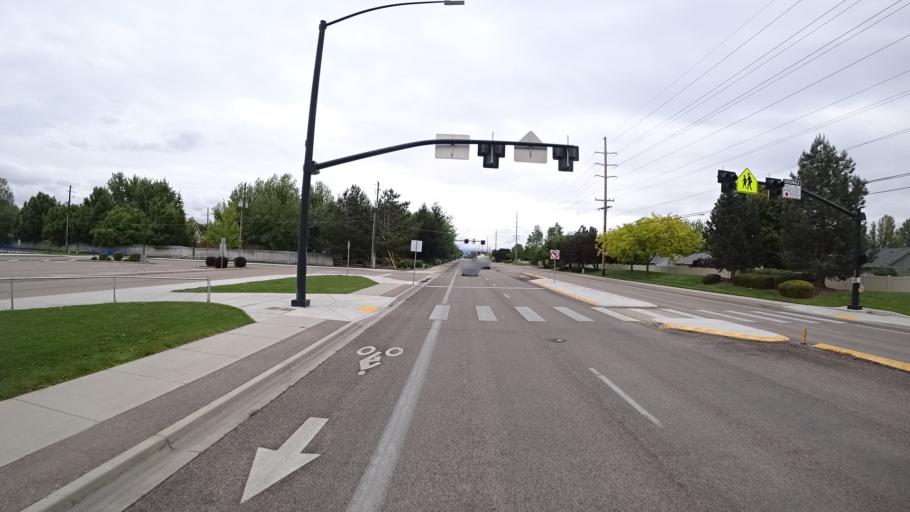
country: US
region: Idaho
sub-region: Ada County
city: Eagle
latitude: 43.6485
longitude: -116.3513
